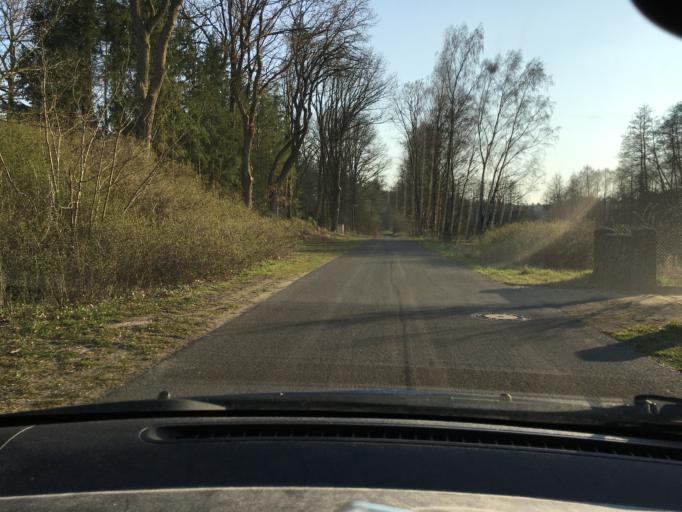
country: DE
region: Lower Saxony
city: Neetze
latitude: 53.2192
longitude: 10.6220
